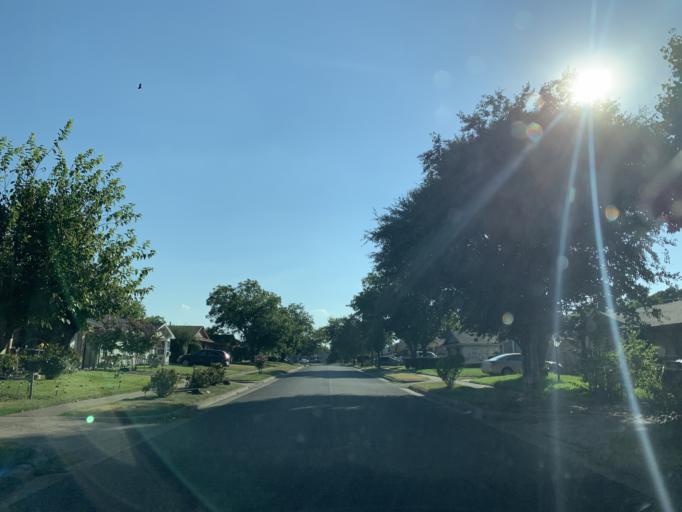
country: US
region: Texas
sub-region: Dallas County
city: Hutchins
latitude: 32.6655
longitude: -96.7647
